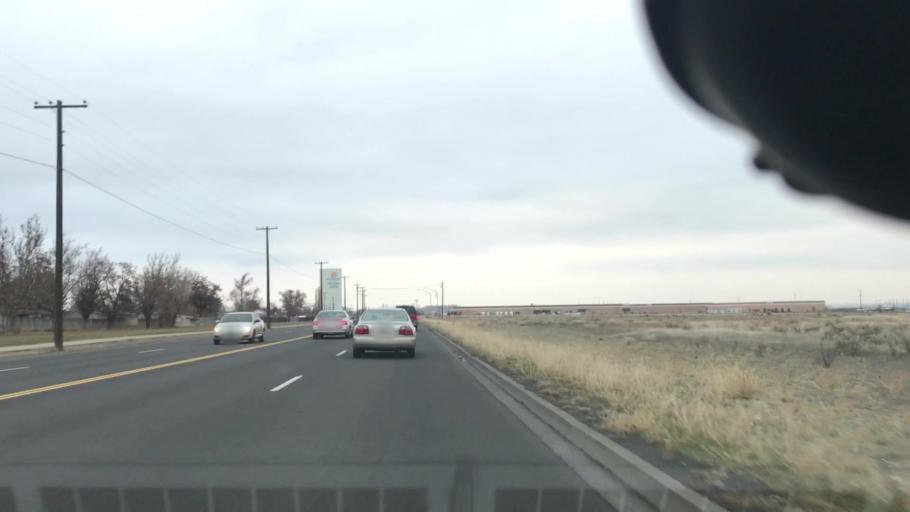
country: US
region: Washington
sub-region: Grant County
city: Moses Lake North
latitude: 47.1651
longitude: -119.3145
